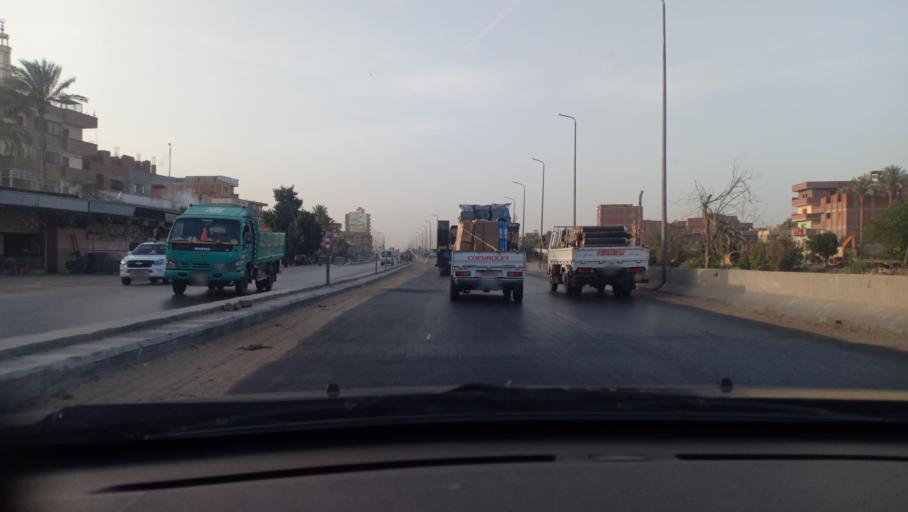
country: EG
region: Muhafazat al Minufiyah
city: Quwaysina
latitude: 30.5441
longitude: 31.2692
